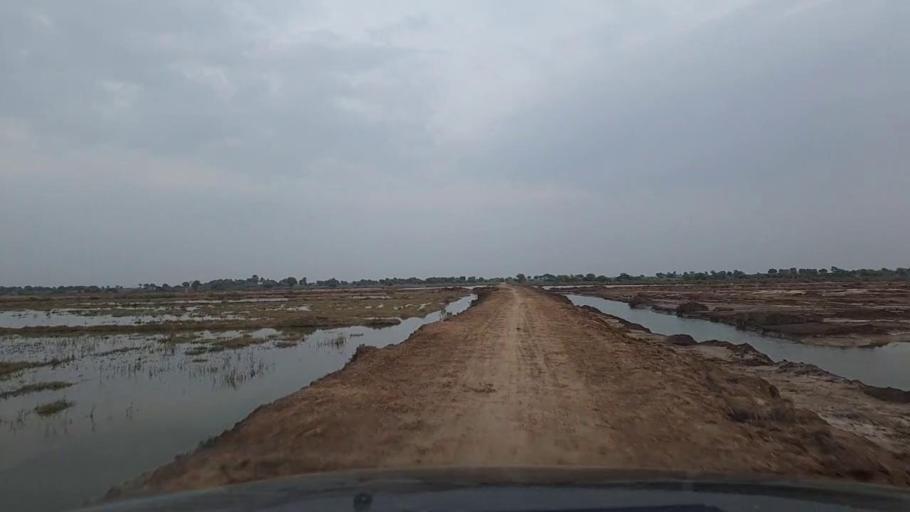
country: PK
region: Sindh
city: Jati
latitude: 24.4976
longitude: 68.3917
